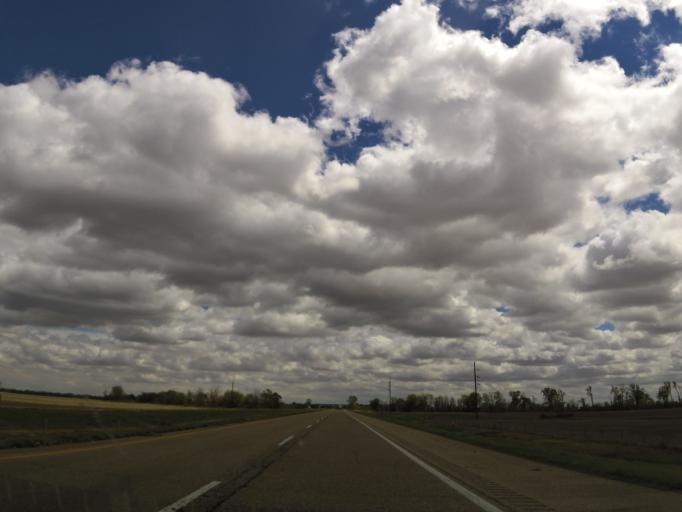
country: US
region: Arkansas
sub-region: Poinsett County
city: Trumann
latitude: 35.6506
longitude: -90.5270
